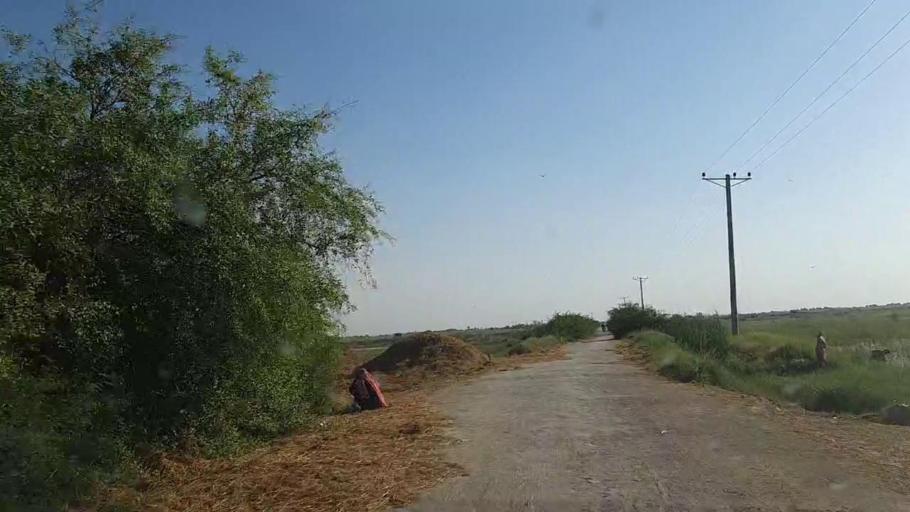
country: PK
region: Sindh
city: Thatta
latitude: 24.6446
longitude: 68.0751
